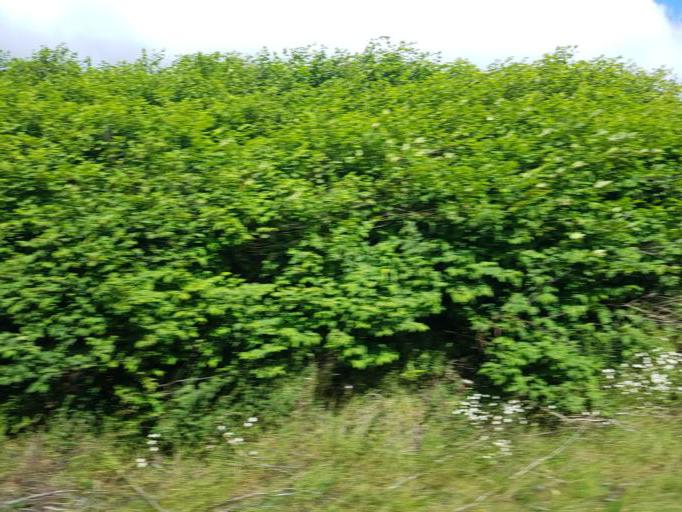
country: GB
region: Scotland
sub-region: North Lanarkshire
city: Cumbernauld
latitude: 55.9811
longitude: -3.9500
